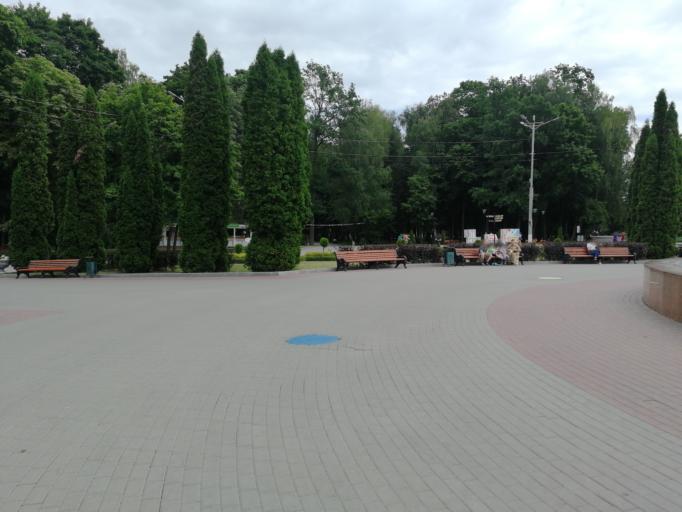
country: RU
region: Tula
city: Tula
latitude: 54.1835
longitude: 37.5922
